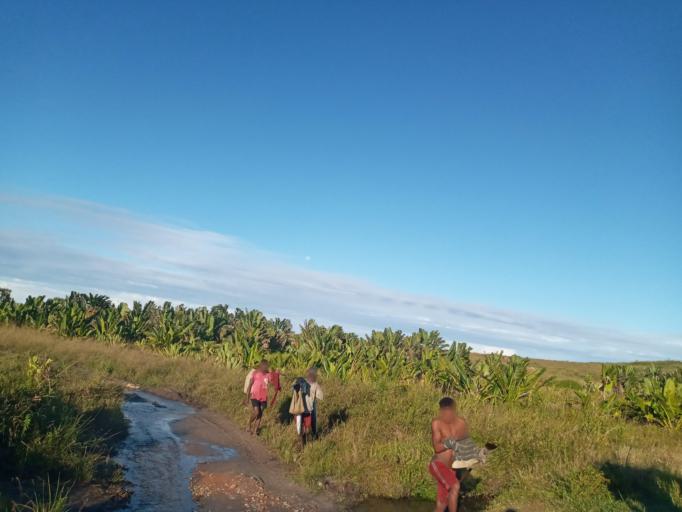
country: MG
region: Anosy
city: Fort Dauphin
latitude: -24.4314
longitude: 47.3020
